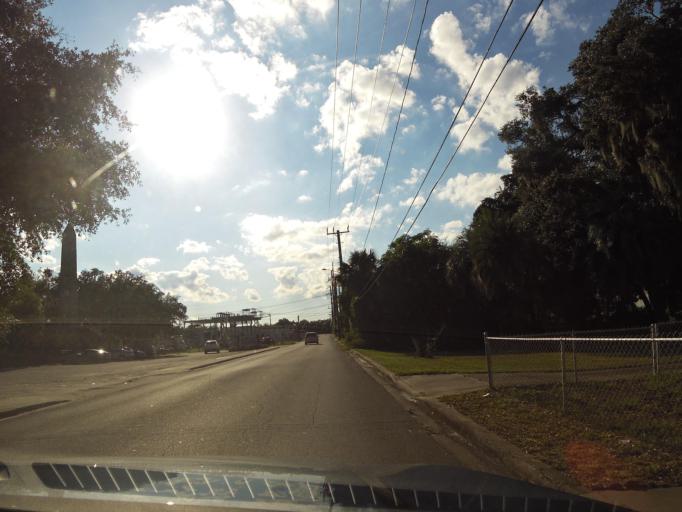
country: US
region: Florida
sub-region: Putnam County
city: Palatka
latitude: 29.6381
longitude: -81.6459
